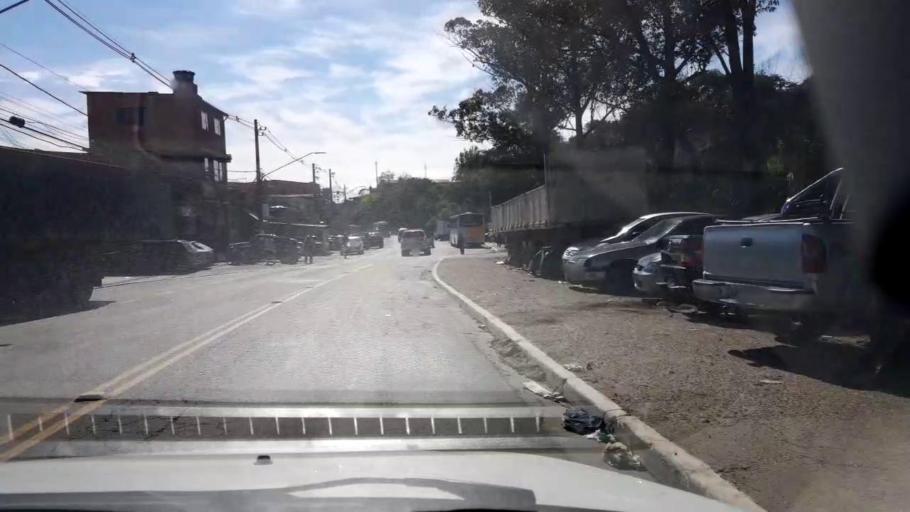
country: BR
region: Sao Paulo
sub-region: Ferraz De Vasconcelos
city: Ferraz de Vasconcelos
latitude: -23.5809
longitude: -46.4154
